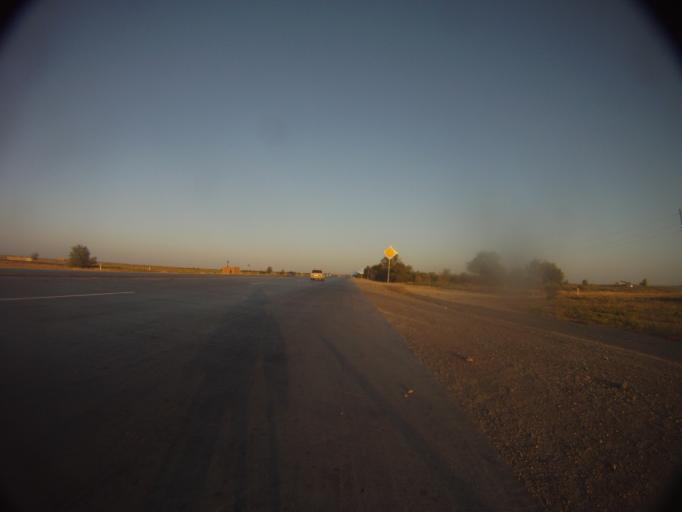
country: KZ
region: Ongtustik Qazaqstan
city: Turkestan
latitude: 43.2716
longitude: 68.3457
